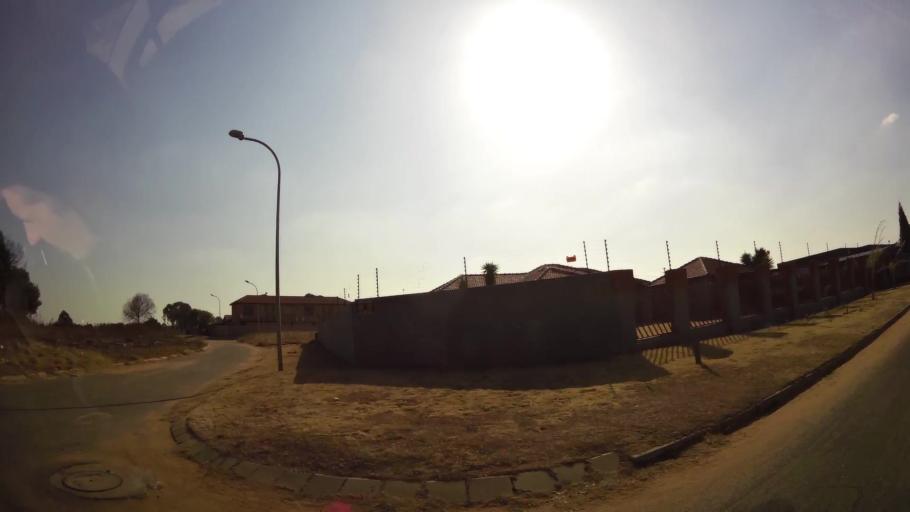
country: ZA
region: Gauteng
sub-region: West Rand District Municipality
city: Randfontein
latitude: -26.1846
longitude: 27.6784
